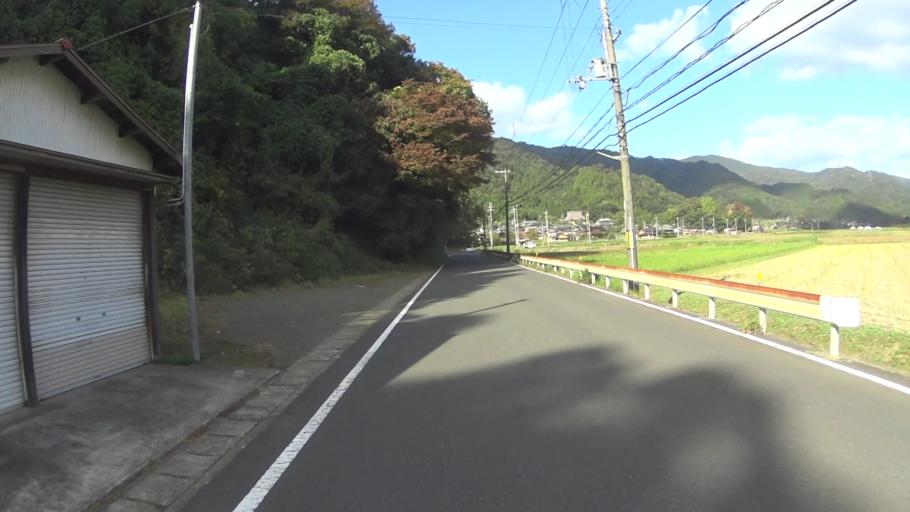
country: JP
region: Kyoto
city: Maizuru
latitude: 35.5173
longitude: 135.4025
